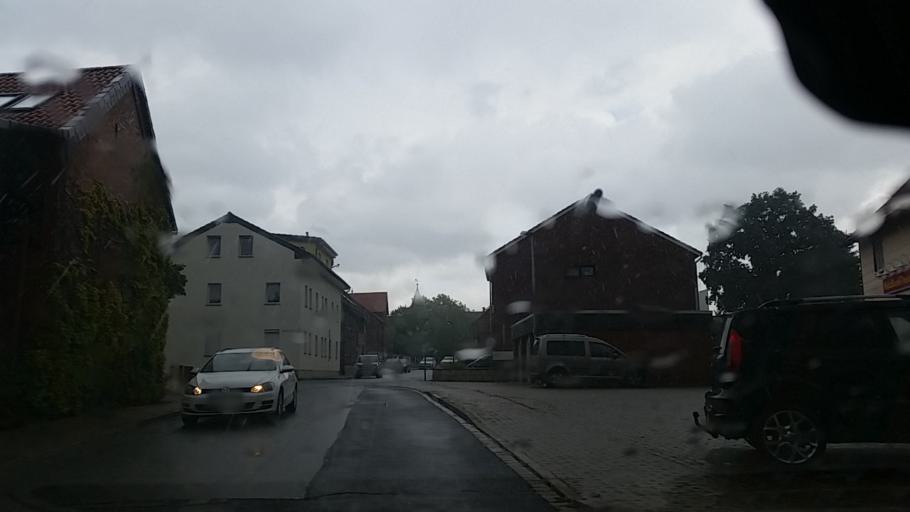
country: DE
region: Lower Saxony
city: Wolfsburg
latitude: 52.4216
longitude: 10.8392
